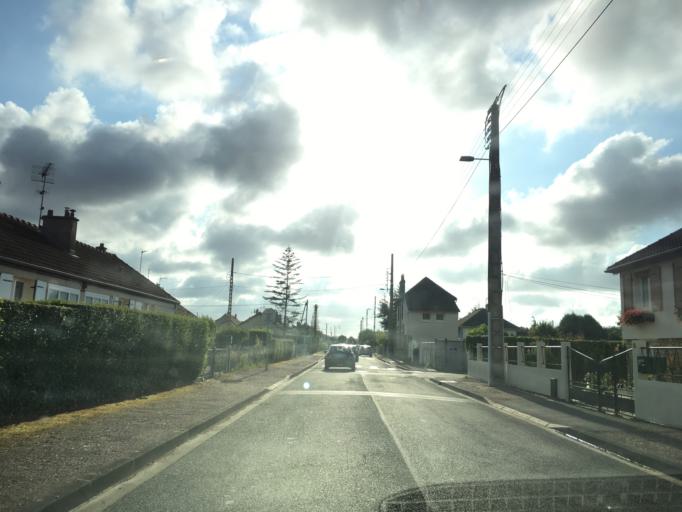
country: FR
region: Lower Normandy
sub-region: Departement du Calvados
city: Dives-sur-Mer
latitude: 49.2877
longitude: -0.1023
